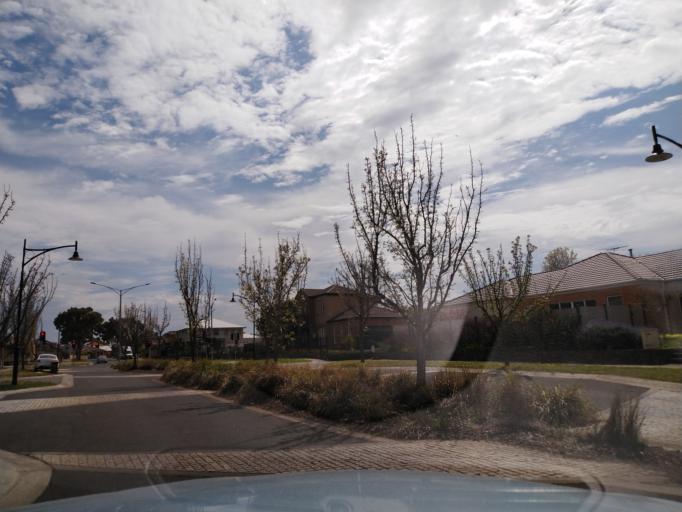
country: AU
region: Victoria
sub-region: Wyndham
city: Hoppers Crossing
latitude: -37.8463
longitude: 144.7081
